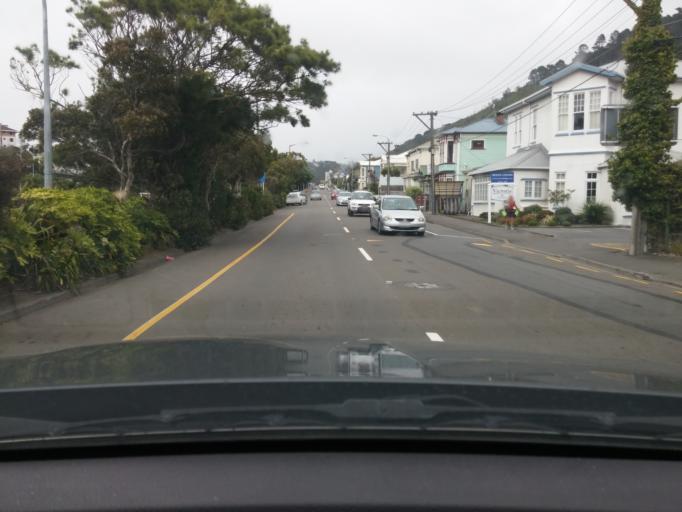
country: NZ
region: Wellington
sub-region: Wellington City
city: Wellington
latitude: -41.2721
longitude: 174.7771
